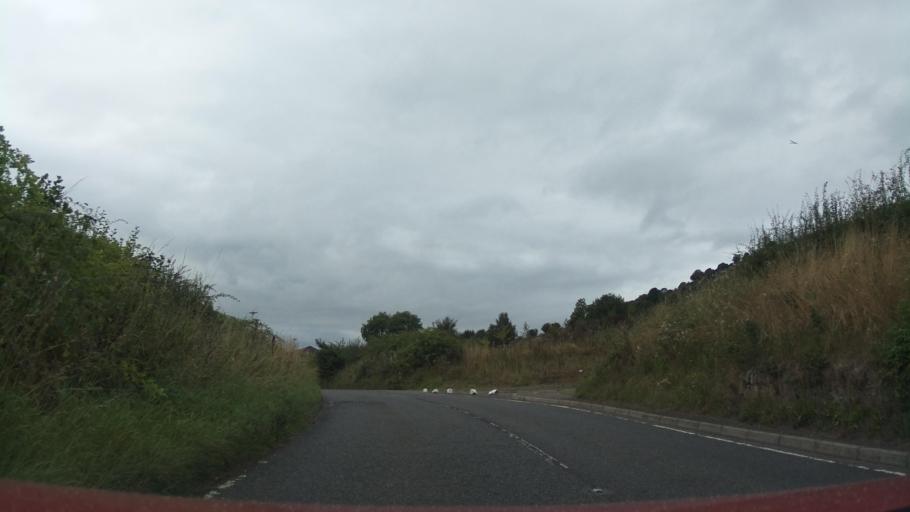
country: GB
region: Scotland
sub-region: Fife
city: Ballingry
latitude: 56.2000
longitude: -3.3043
